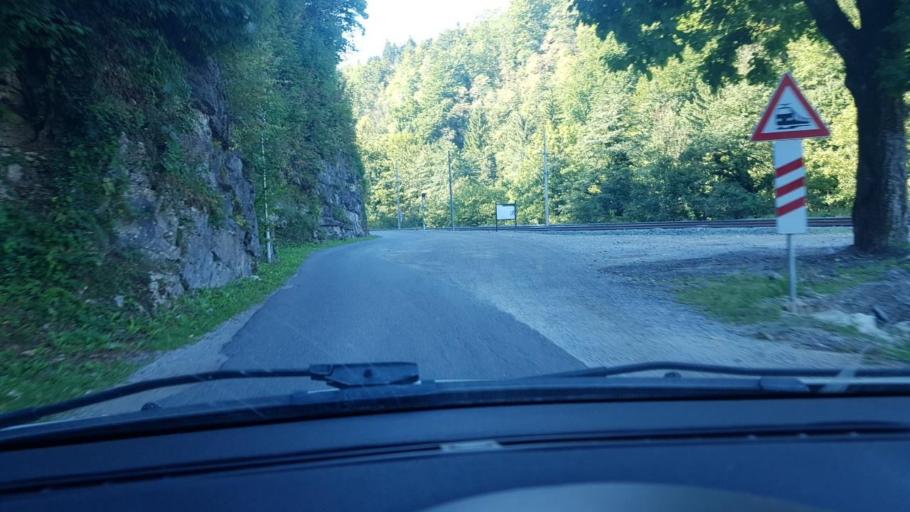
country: HR
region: Primorsko-Goranska
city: Vrbovsko
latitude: 45.3713
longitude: 15.0719
